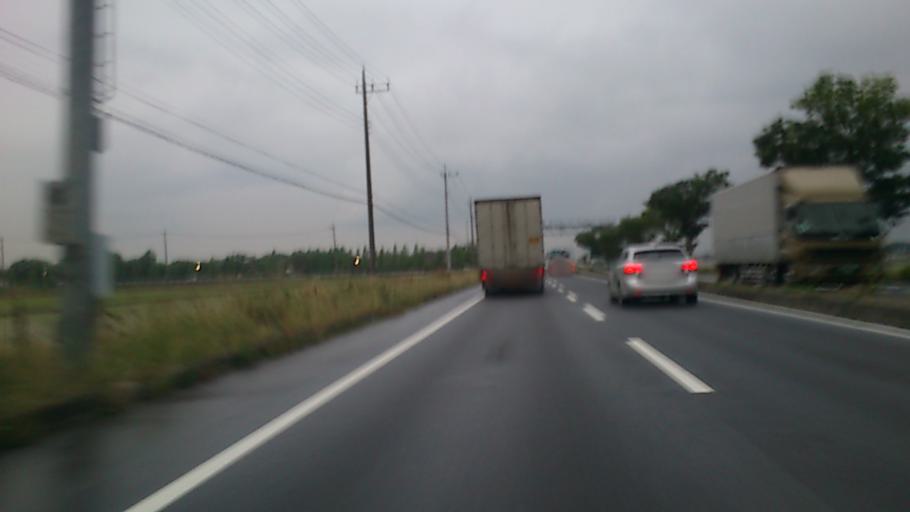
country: JP
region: Saitama
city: Gyoda
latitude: 36.1566
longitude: 139.4577
